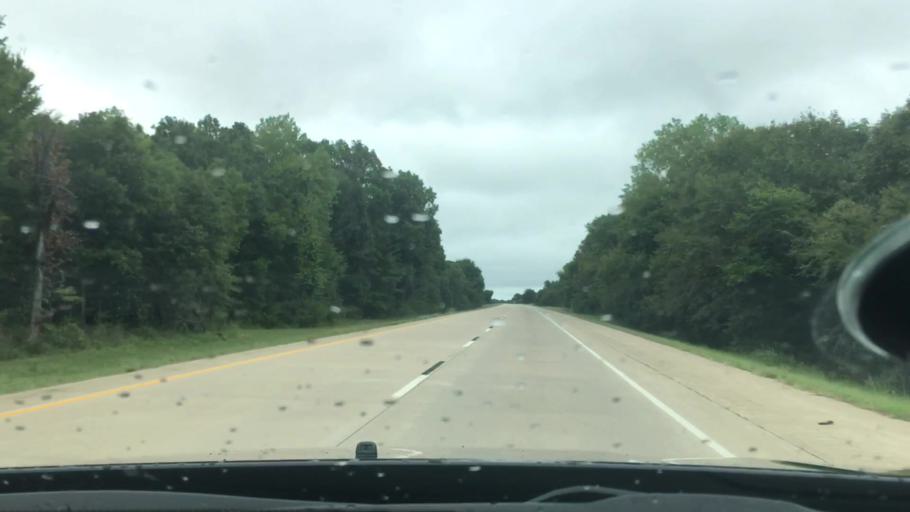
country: US
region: Oklahoma
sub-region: Okmulgee County
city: Morris
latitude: 35.4501
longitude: -95.7349
